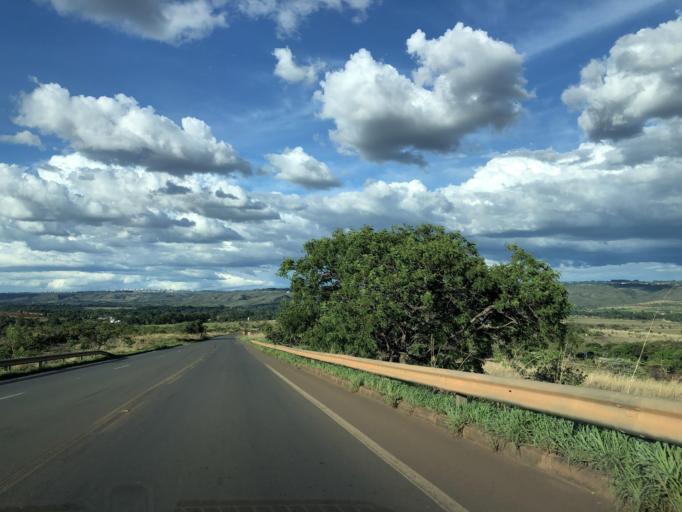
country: BR
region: Goias
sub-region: Luziania
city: Luziania
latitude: -16.0128
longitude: -48.1359
